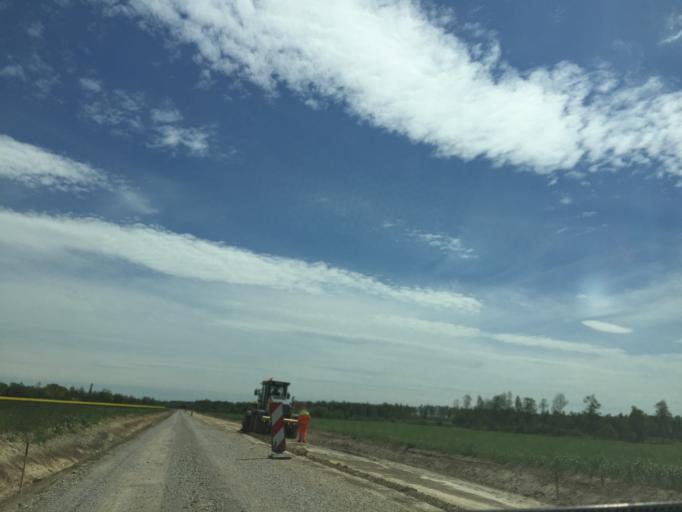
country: LT
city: Linkuva
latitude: 56.0549
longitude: 24.0950
